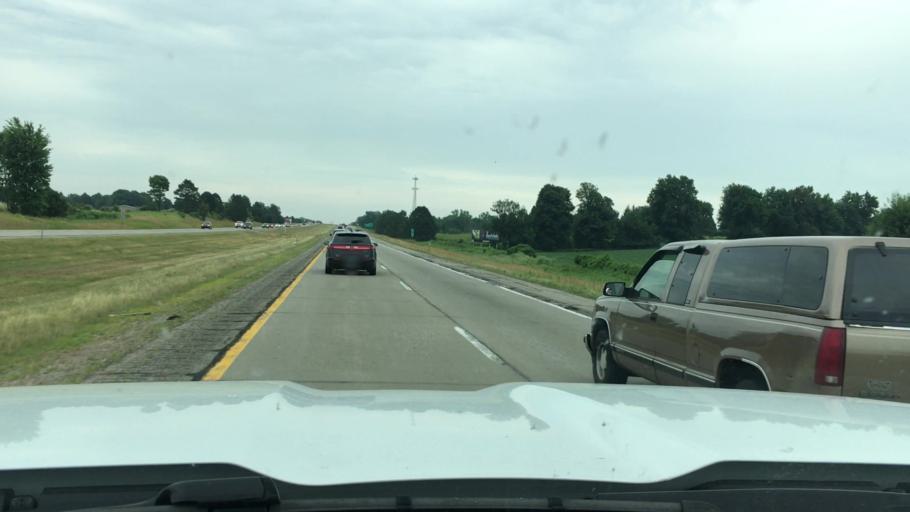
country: US
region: Michigan
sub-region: Eaton County
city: Grand Ledge
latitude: 42.8166
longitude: -84.8009
